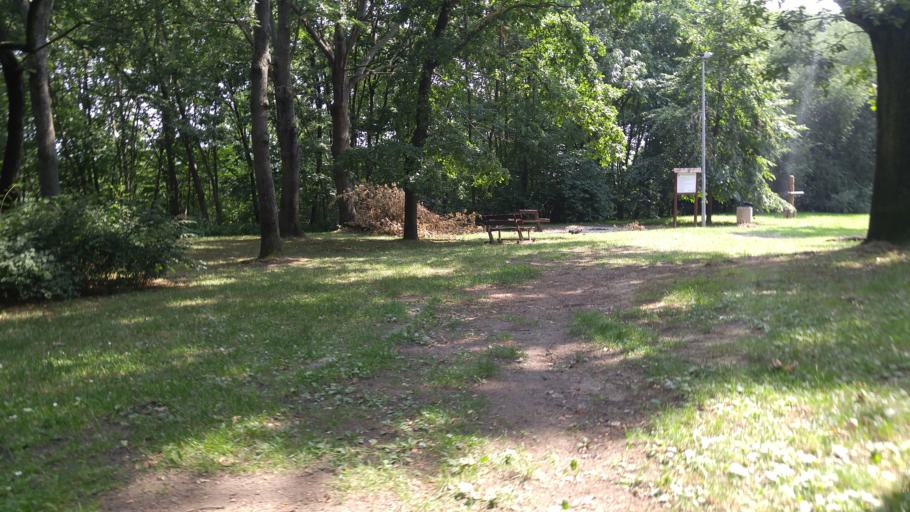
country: CZ
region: Central Bohemia
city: Horomerice
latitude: 50.0930
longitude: 14.3456
